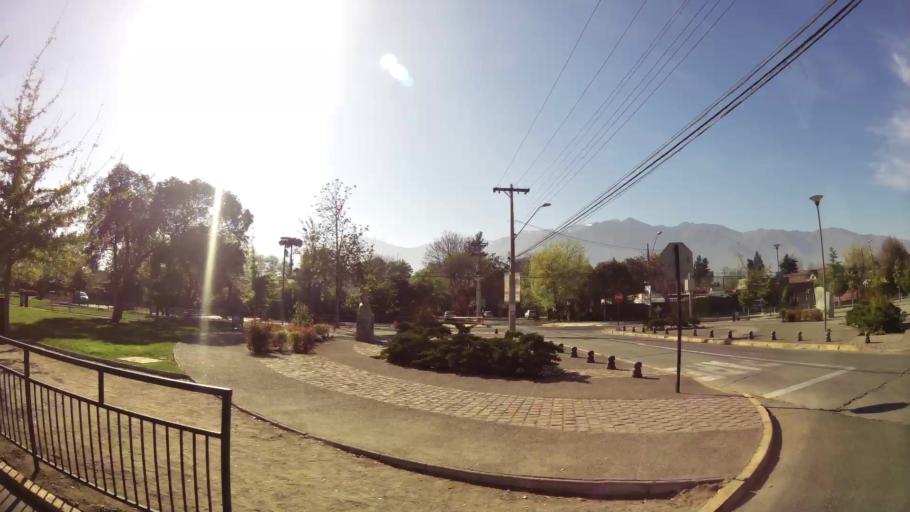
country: CL
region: Santiago Metropolitan
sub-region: Provincia de Santiago
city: Villa Presidente Frei, Nunoa, Santiago, Chile
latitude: -33.4375
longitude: -70.5564
